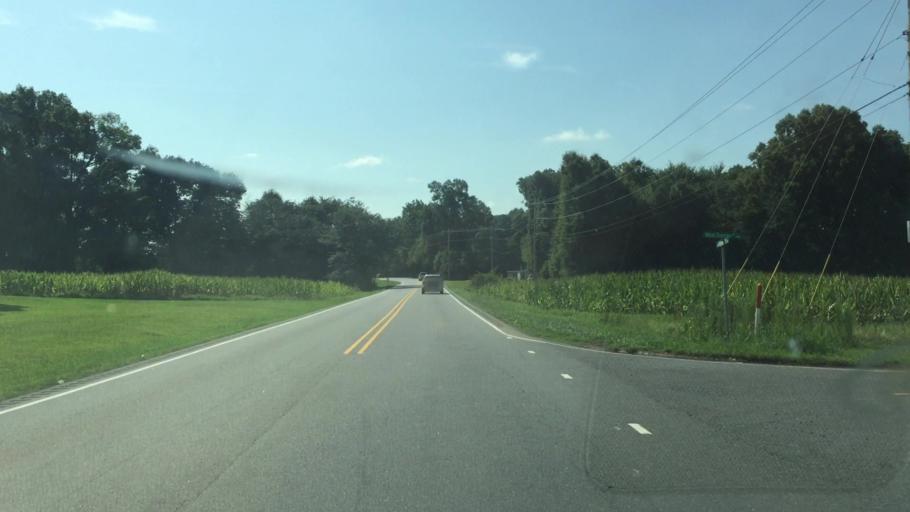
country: US
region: North Carolina
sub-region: Union County
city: Fairview
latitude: 35.1551
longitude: -80.5615
